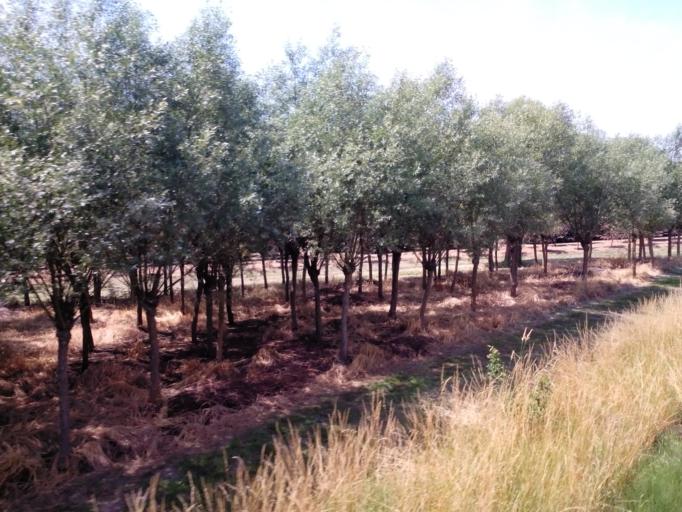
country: BE
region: Flanders
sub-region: Provincie Antwerpen
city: Berlaar
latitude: 51.0976
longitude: 4.6654
